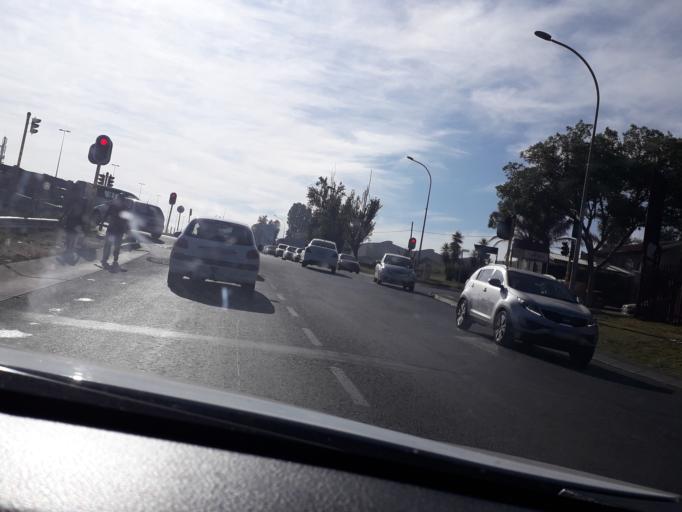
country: ZA
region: Gauteng
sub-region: Ekurhuleni Metropolitan Municipality
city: Germiston
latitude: -26.1651
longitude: 28.1799
